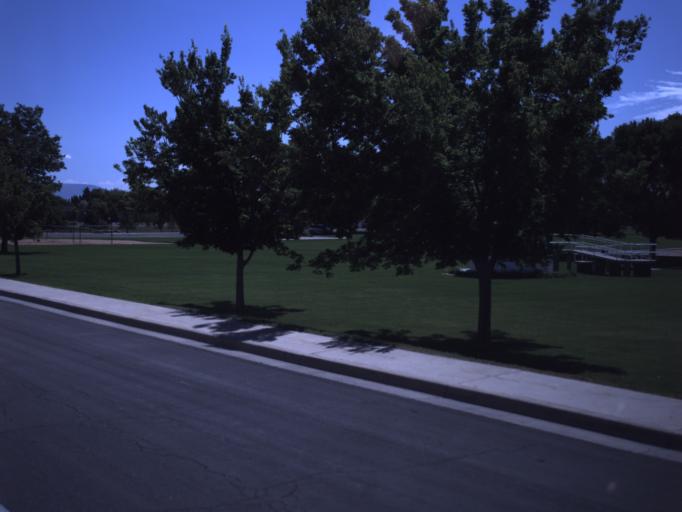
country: US
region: Utah
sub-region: Uintah County
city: Vernal
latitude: 40.4628
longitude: -109.5472
